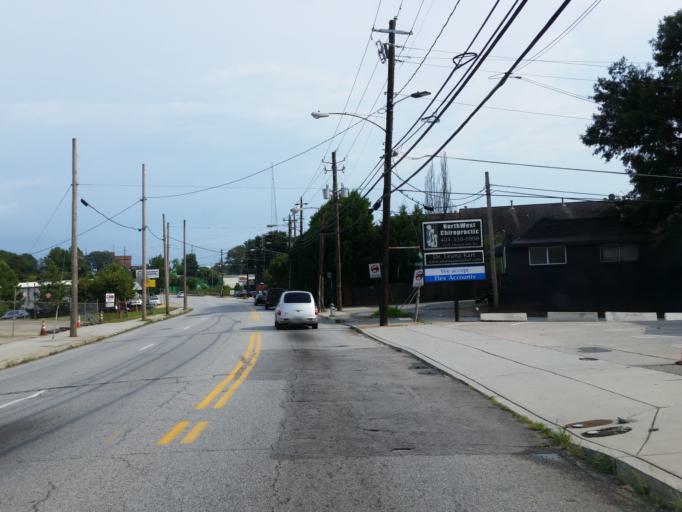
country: US
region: Georgia
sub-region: Fulton County
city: Atlanta
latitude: 33.7972
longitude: -84.4162
